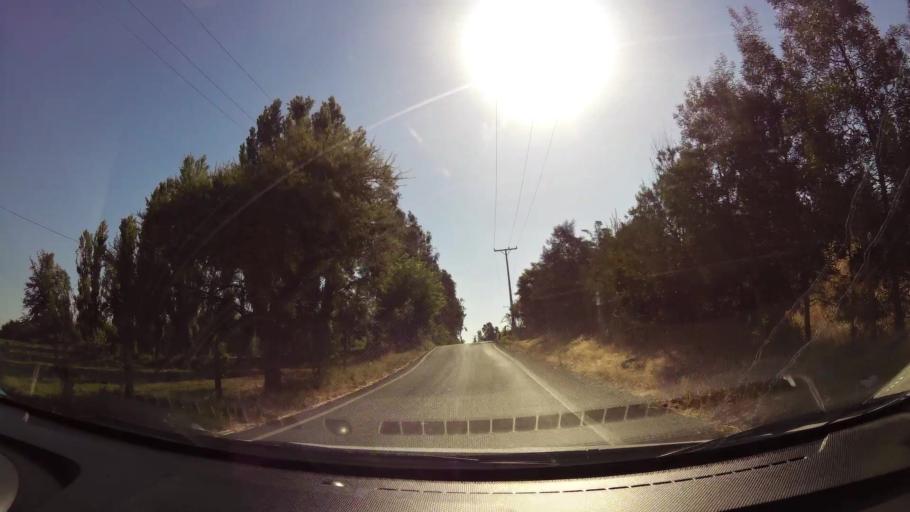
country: CL
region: Maule
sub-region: Provincia de Talca
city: Talca
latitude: -35.4063
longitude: -71.5981
